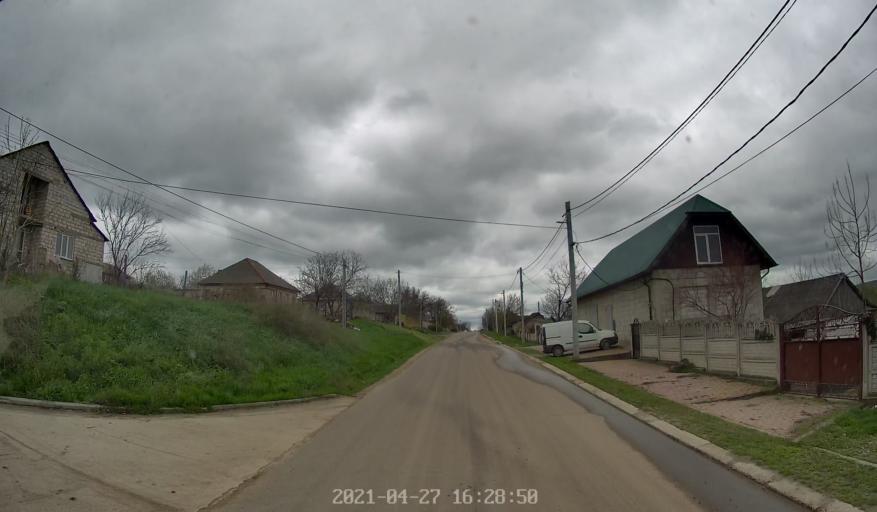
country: MD
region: Chisinau
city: Singera
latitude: 46.9701
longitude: 29.0456
